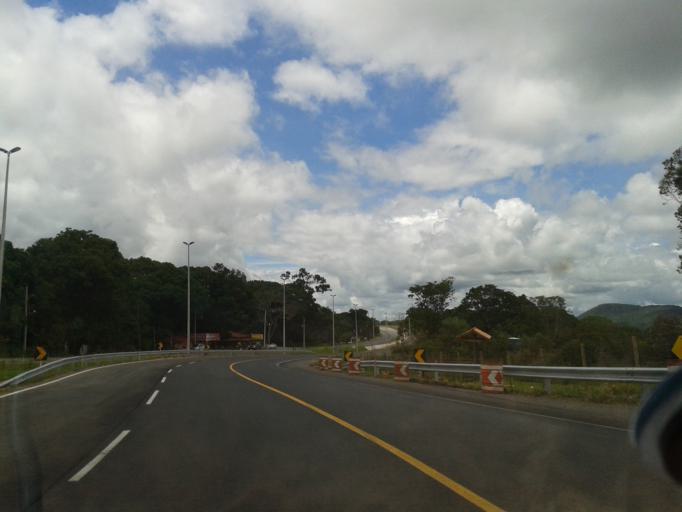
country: BR
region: Goias
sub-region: Goias
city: Goias
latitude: -15.9864
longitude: -50.0776
